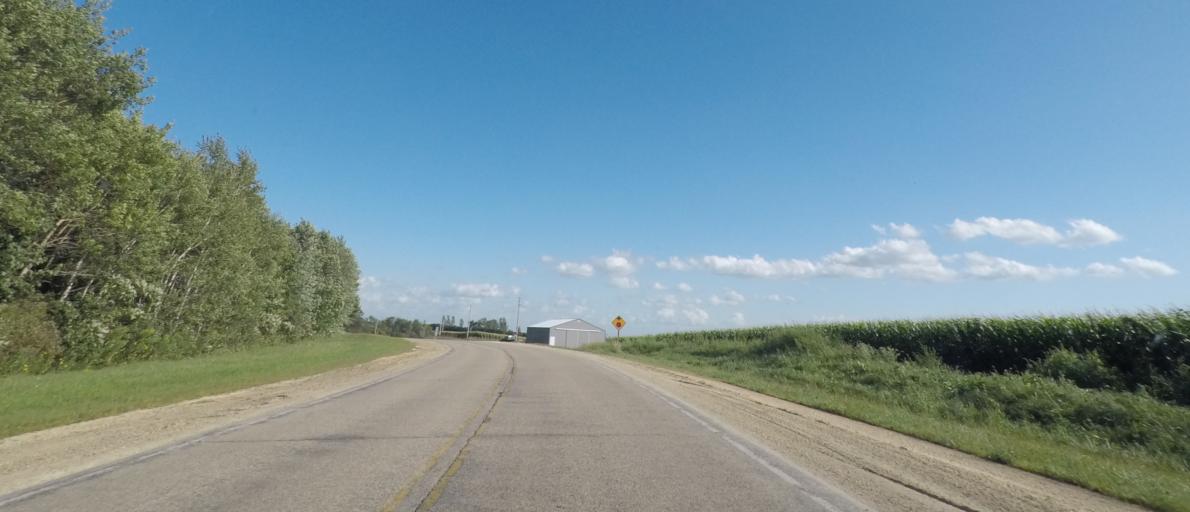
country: US
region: Wisconsin
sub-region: Iowa County
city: Dodgeville
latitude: 42.9730
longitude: -90.0483
